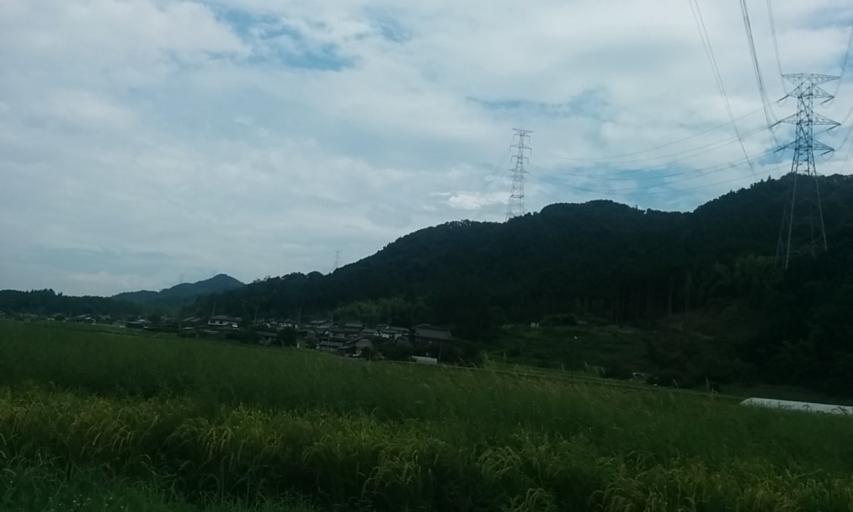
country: JP
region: Kyoto
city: Ayabe
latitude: 35.3456
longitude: 135.2195
